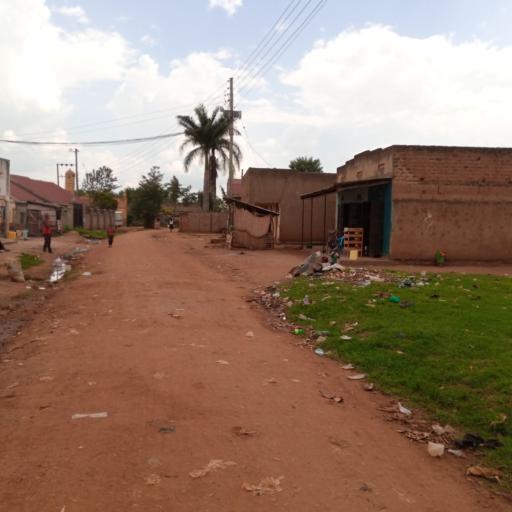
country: UG
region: Eastern Region
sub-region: Mbale District
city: Mbale
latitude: 1.0935
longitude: 34.1677
